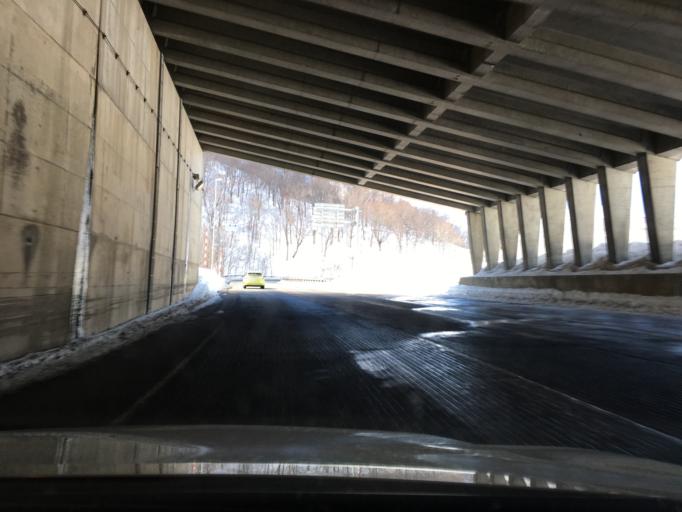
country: JP
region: Yamagata
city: Tsuruoka
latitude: 38.4788
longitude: 139.9941
